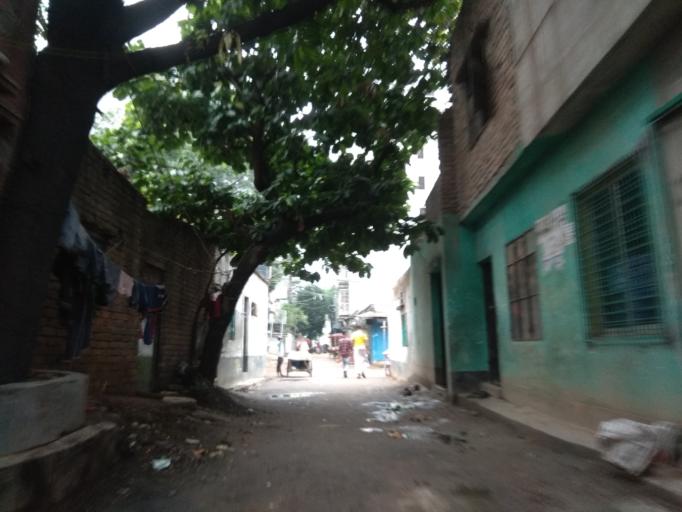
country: BD
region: Dhaka
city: Tungi
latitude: 23.8240
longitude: 90.3755
